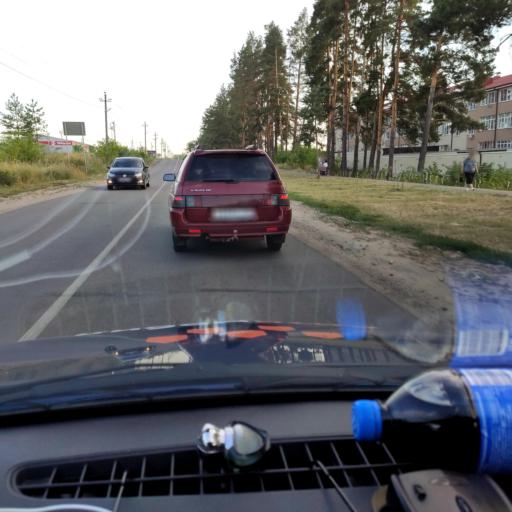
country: RU
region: Voronezj
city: Podgornoye
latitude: 51.8147
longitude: 39.1407
